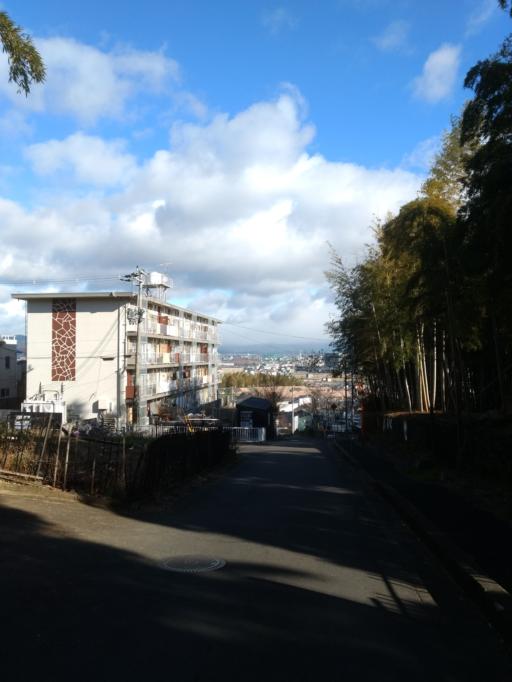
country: JP
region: Kyoto
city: Muko
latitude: 34.9547
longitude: 135.6945
